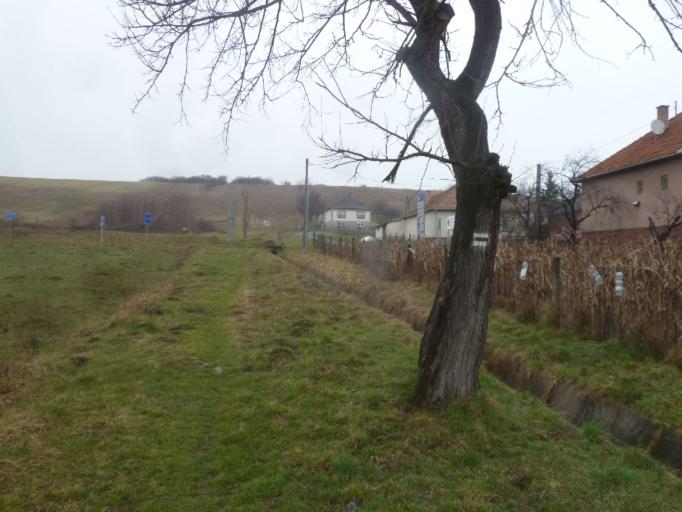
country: HU
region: Nograd
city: Matranovak
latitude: 48.1496
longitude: 19.9508
